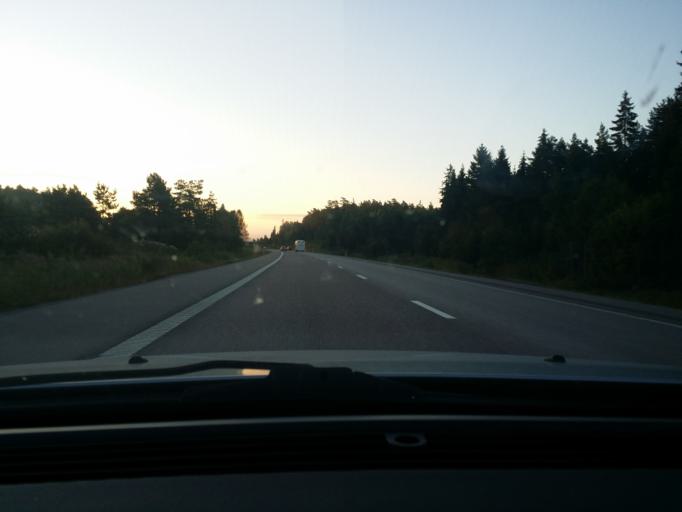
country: SE
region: Uppsala
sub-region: Enkopings Kommun
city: Grillby
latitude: 59.6418
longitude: 17.2111
